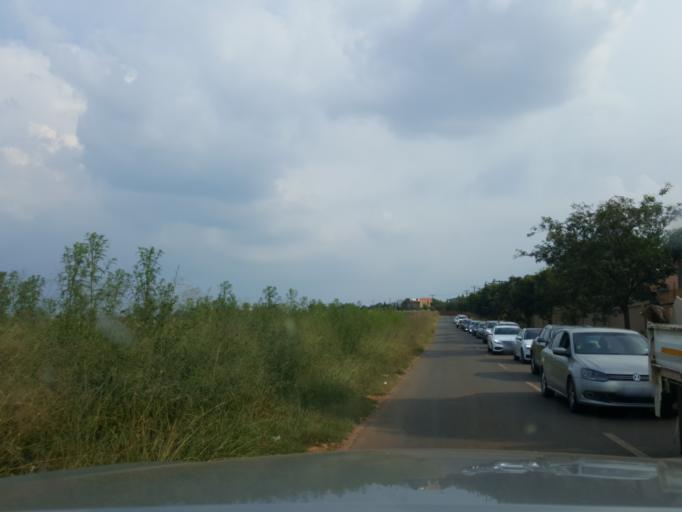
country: ZA
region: Gauteng
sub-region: City of Tshwane Metropolitan Municipality
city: Centurion
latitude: -25.8527
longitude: 28.3254
